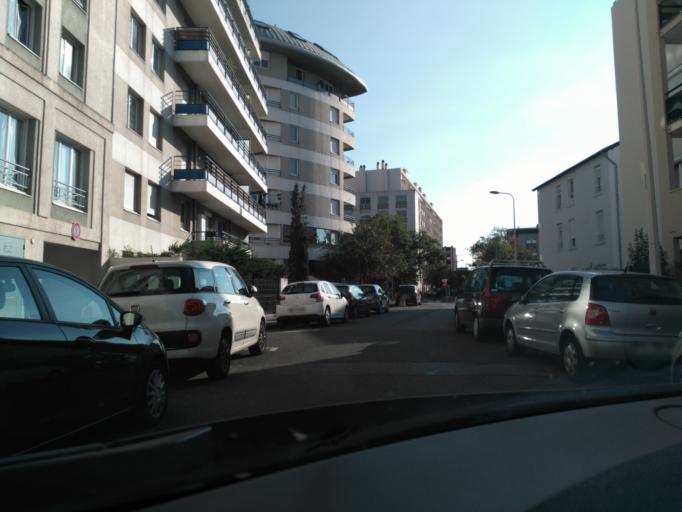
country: FR
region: Rhone-Alpes
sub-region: Departement du Rhone
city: Lyon
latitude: 45.7449
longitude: 4.8616
